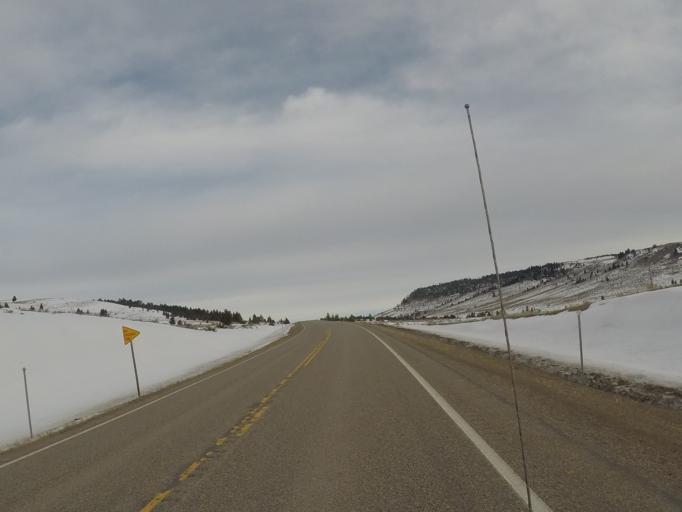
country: US
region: Montana
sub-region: Meagher County
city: White Sulphur Springs
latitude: 46.6385
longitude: -110.8727
